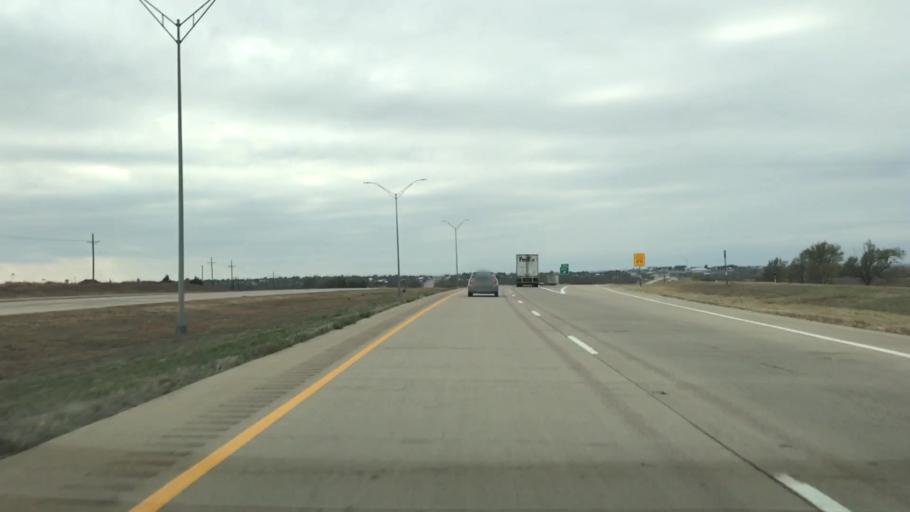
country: US
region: Texas
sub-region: Wheeler County
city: Shamrock
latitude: 35.2271
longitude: -100.2182
